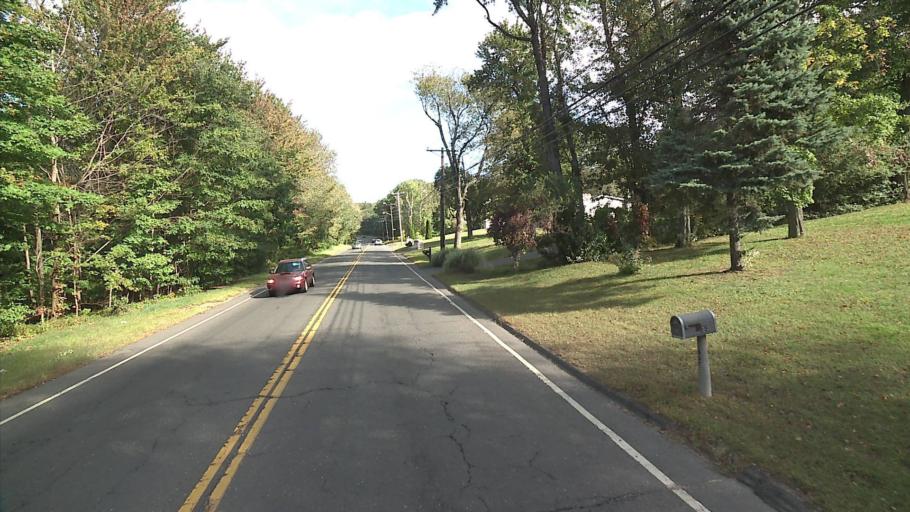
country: US
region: Connecticut
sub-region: Hartford County
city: Bristol
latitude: 41.6453
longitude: -72.9638
